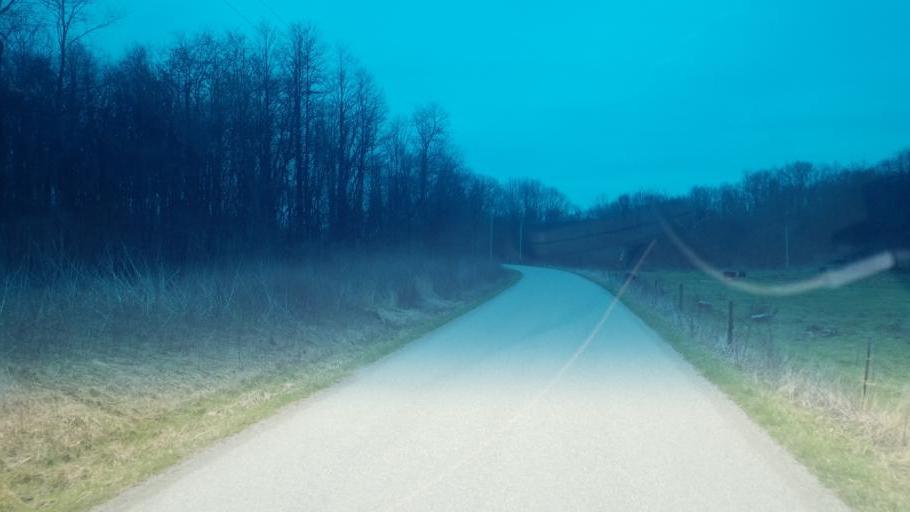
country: US
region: Ohio
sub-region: Knox County
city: Centerburg
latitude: 40.3585
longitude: -82.6489
